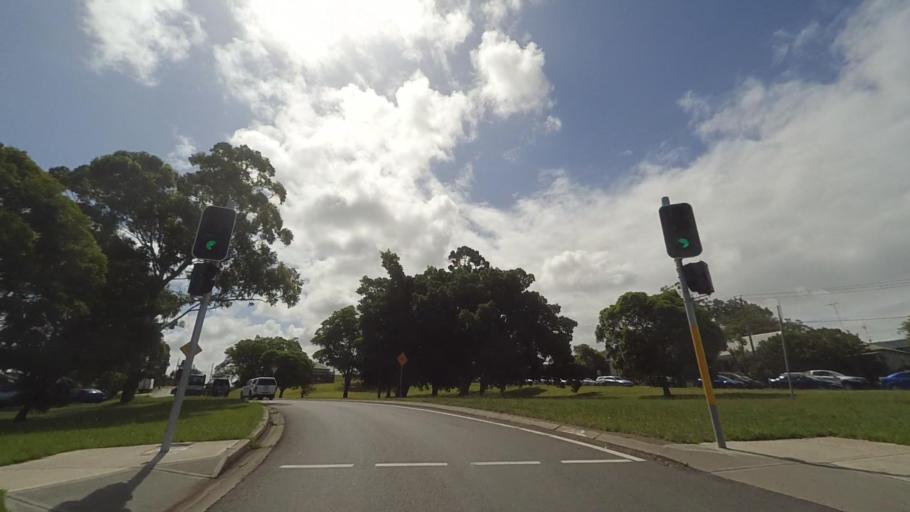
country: AU
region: New South Wales
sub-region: Newcastle
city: North Lambton
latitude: -32.9094
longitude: 151.7049
